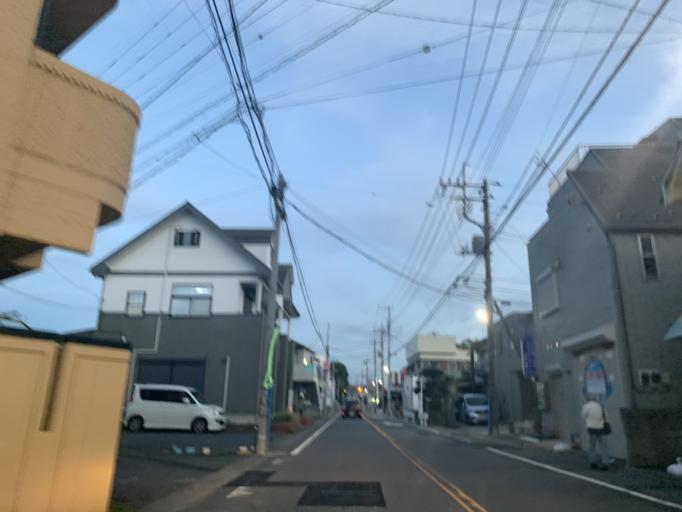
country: JP
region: Chiba
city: Nagareyama
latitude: 35.8987
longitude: 139.9168
